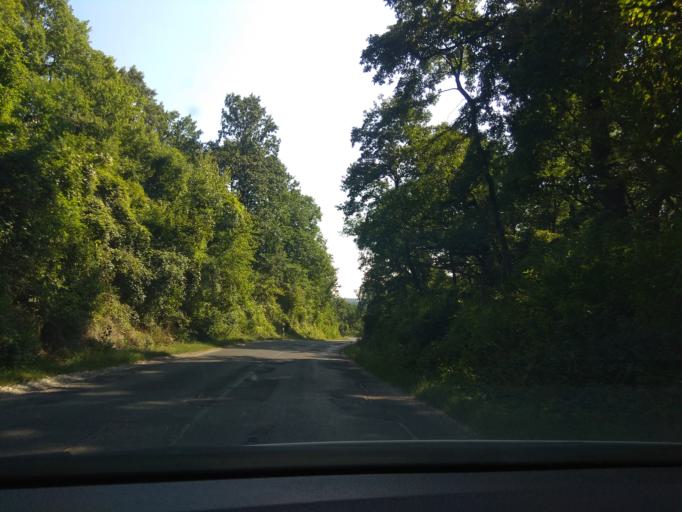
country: HU
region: Borsod-Abauj-Zemplen
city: Harsany
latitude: 48.0217
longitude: 20.7630
